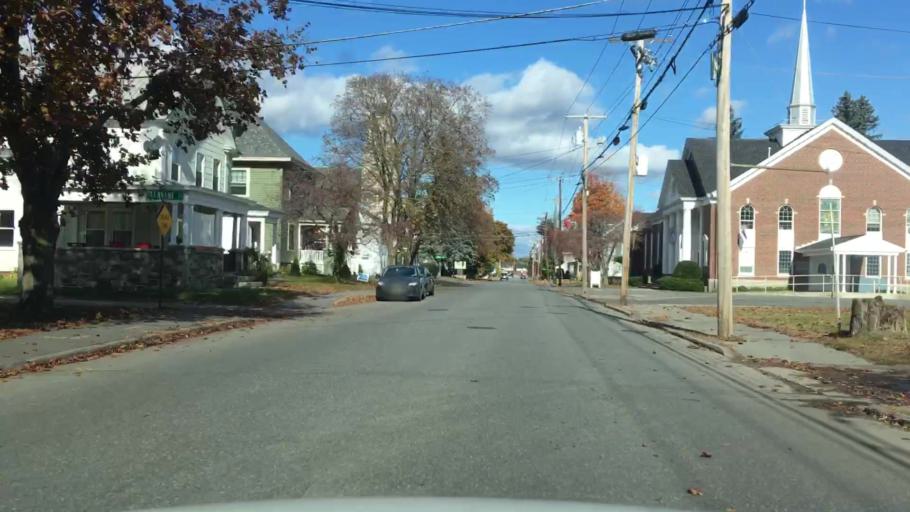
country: US
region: Maine
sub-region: Kennebec County
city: Waterville
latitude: 44.5523
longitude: -69.6349
